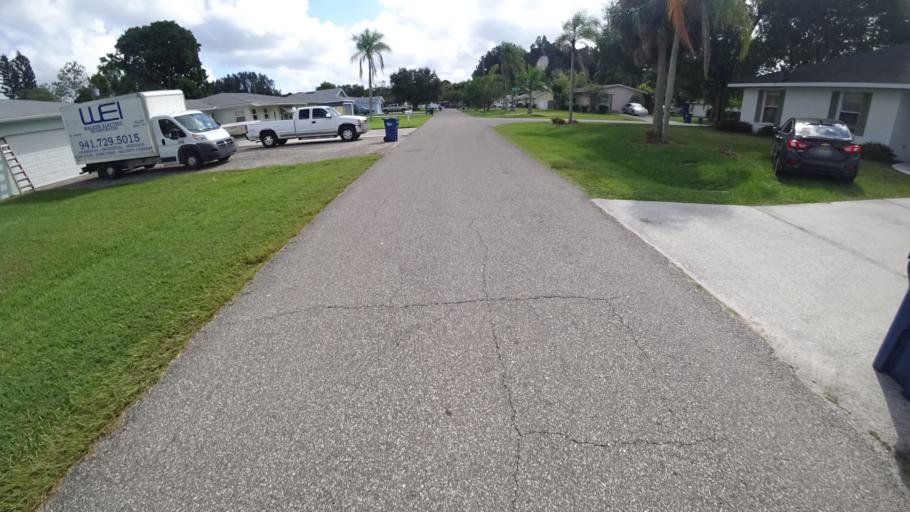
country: US
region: Florida
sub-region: Manatee County
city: Memphis
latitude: 27.5520
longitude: -82.5674
